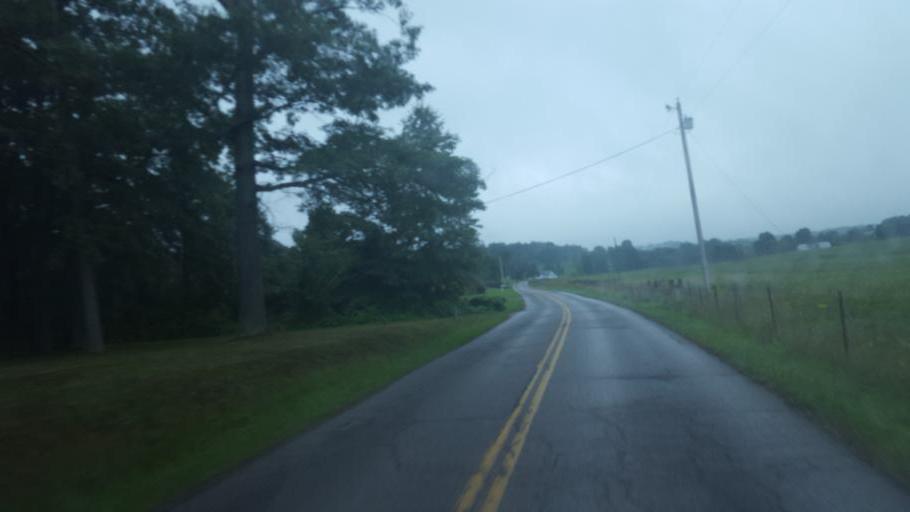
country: US
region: Ohio
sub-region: Jackson County
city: Oak Hill
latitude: 38.9319
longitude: -82.6042
